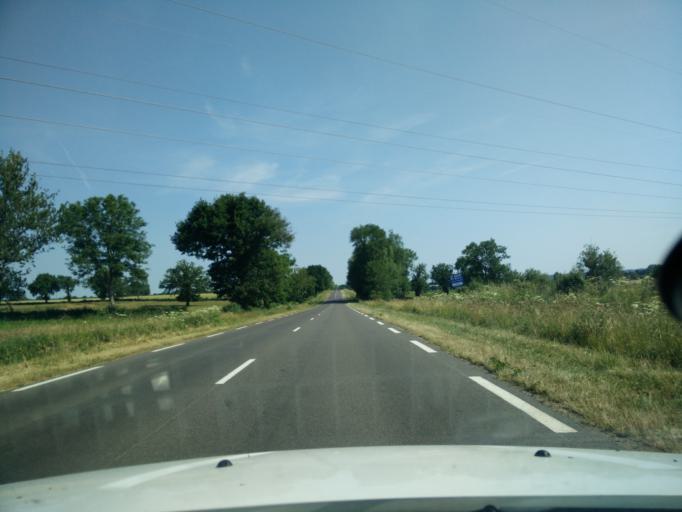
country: FR
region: Auvergne
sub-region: Departement de l'Allier
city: Toulon-sur-Allier
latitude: 46.4991
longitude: 3.3162
